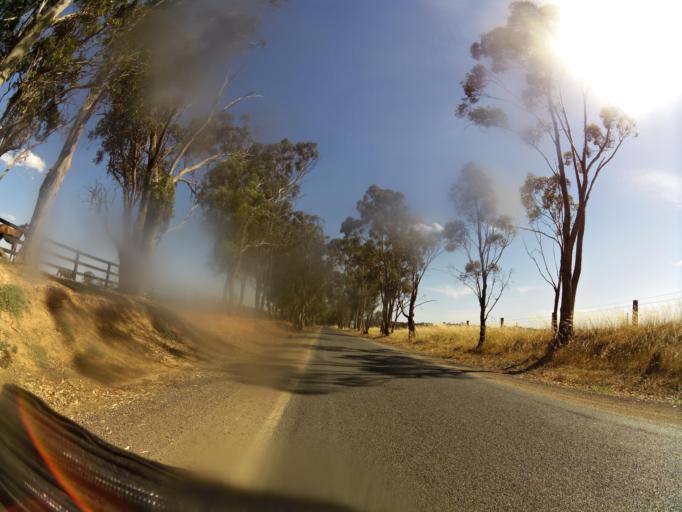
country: AU
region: Victoria
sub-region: Campaspe
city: Kyabram
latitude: -36.8608
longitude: 145.0882
